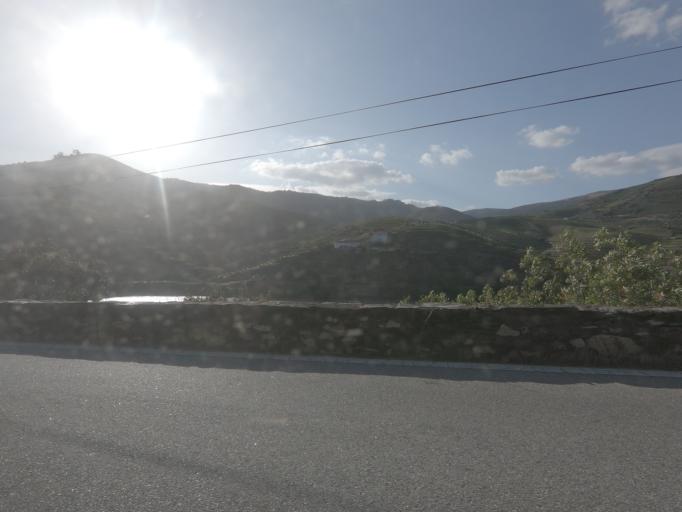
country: PT
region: Viseu
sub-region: Tabuaco
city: Tabuaco
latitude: 41.1637
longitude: -7.5705
